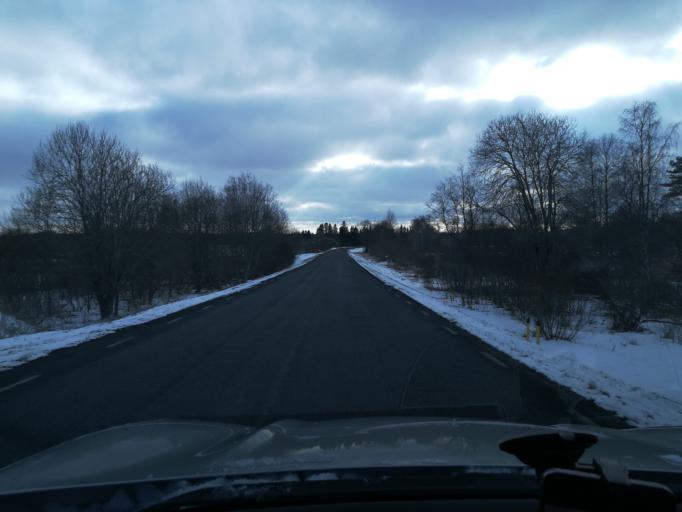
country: EE
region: Harju
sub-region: Keila linn
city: Keila
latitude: 59.4184
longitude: 24.4184
